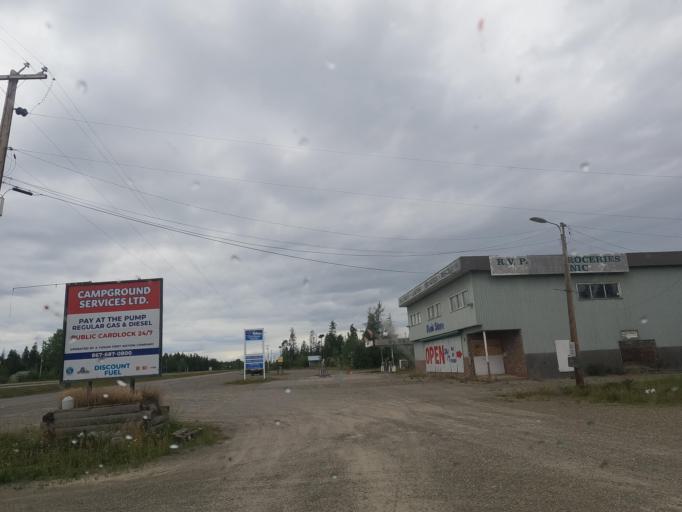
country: CA
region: Yukon
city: Watson Lake
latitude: 60.0501
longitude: -128.6545
